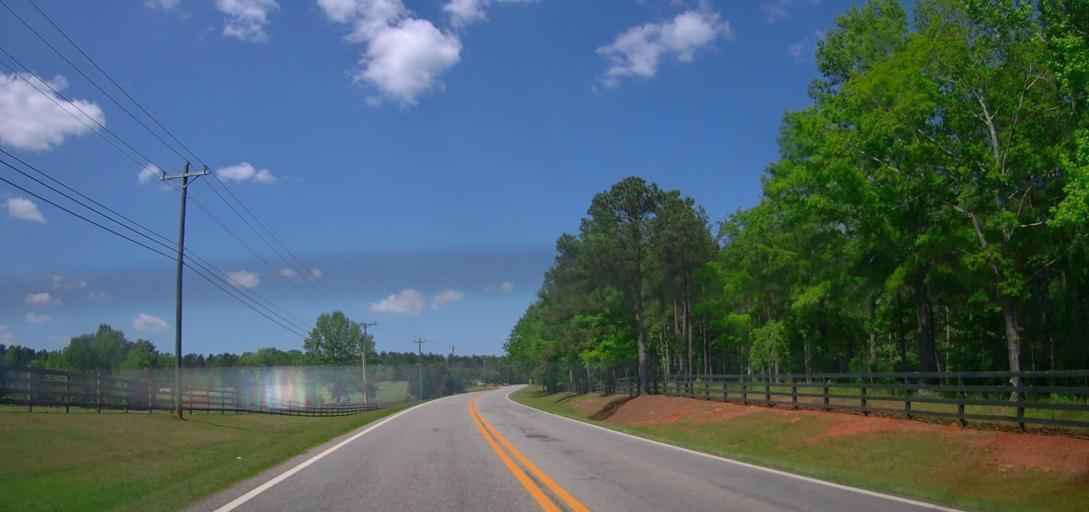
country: US
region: Georgia
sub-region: Putnam County
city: Eatonton
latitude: 33.2996
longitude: -83.3036
